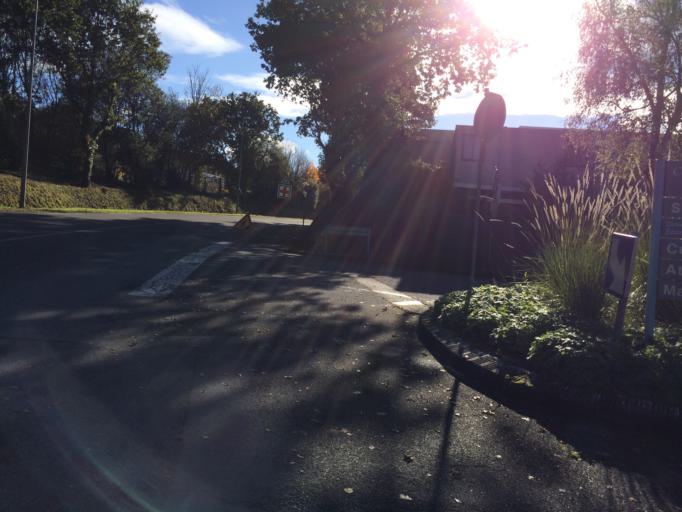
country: FR
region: Brittany
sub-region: Departement du Finistere
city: Pencran
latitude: 48.4489
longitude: -4.2338
